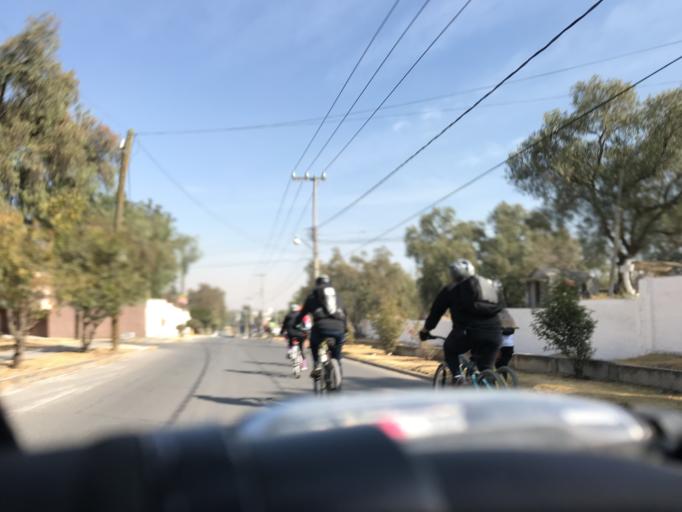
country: MX
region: Mexico
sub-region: Tecamac
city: Ojo de Agua
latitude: 19.6727
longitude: -99.0075
